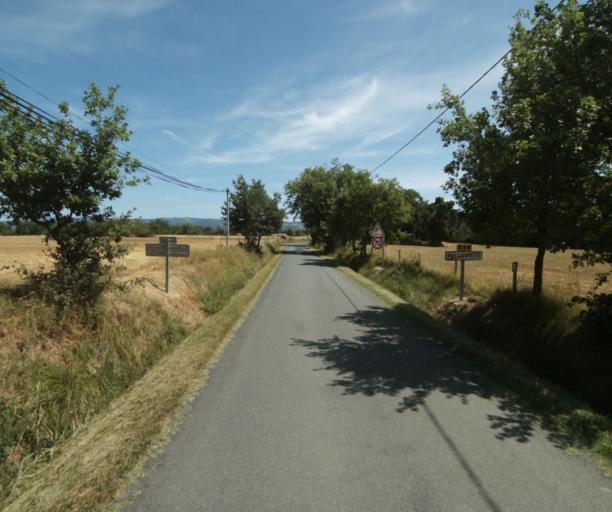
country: FR
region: Midi-Pyrenees
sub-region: Departement de la Haute-Garonne
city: Revel
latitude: 43.5014
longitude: 2.0017
